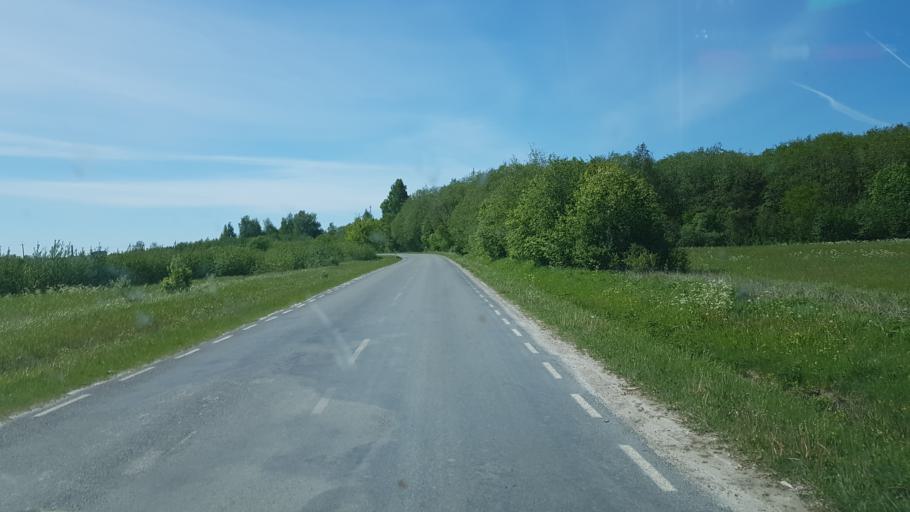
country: EE
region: Saare
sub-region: Kuressaare linn
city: Kuressaare
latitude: 58.2802
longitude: 22.5028
